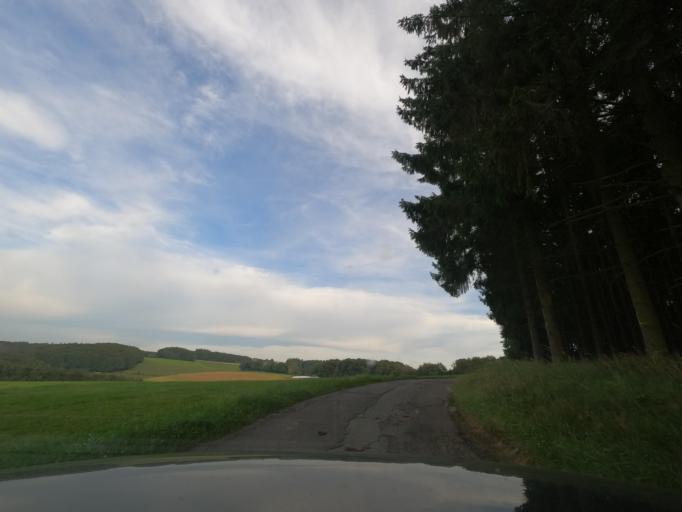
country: DE
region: North Rhine-Westphalia
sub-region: Regierungsbezirk Arnsberg
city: Herscheid
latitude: 51.2037
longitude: 7.7414
